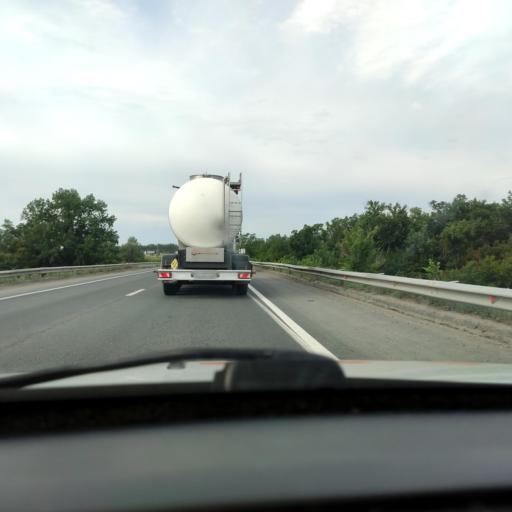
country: RU
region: Samara
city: Mirnyy
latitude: 53.5263
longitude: 50.3243
